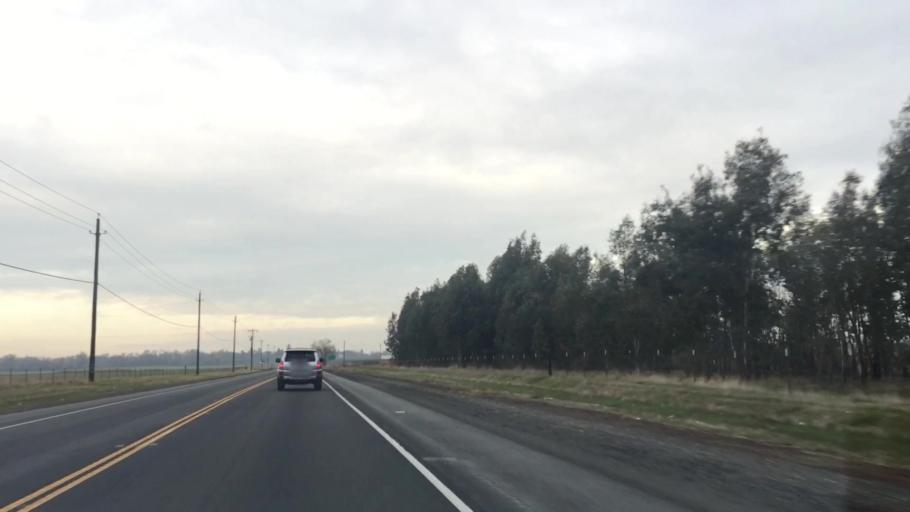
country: US
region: California
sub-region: Butte County
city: Palermo
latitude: 39.4121
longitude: -121.6048
